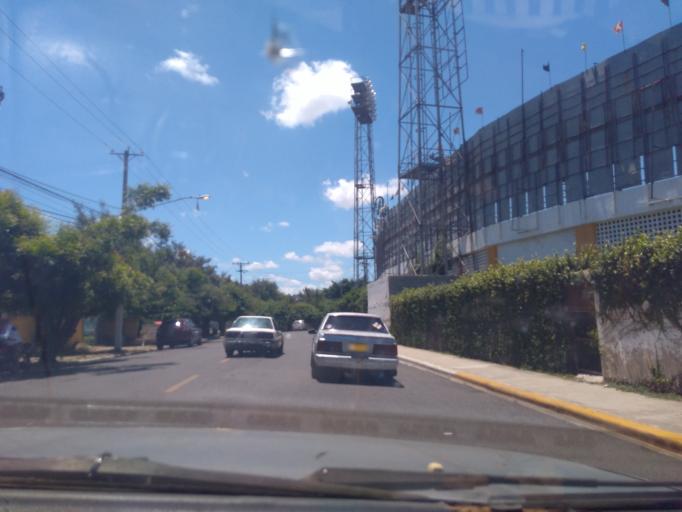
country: DO
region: Santiago
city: Santiago de los Caballeros
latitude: 19.4682
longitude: -70.7092
